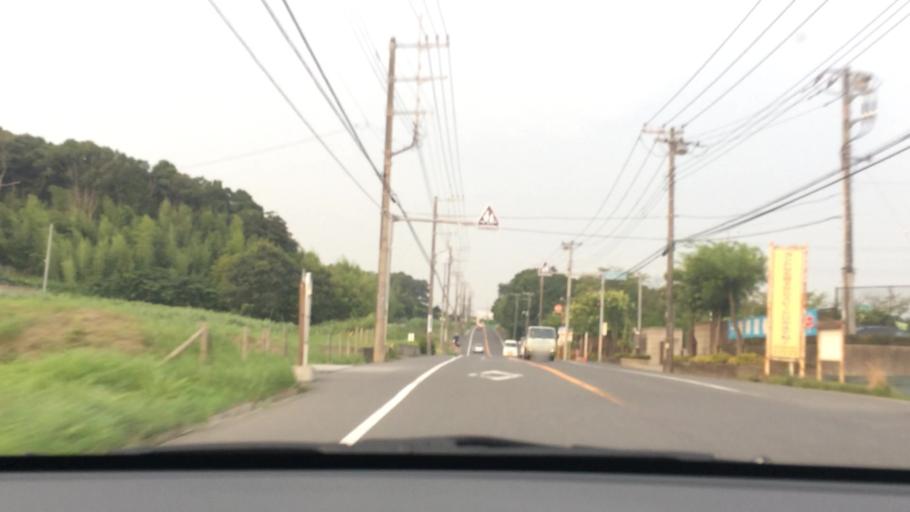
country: JP
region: Chiba
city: Nagareyama
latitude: 35.8712
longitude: 139.9118
